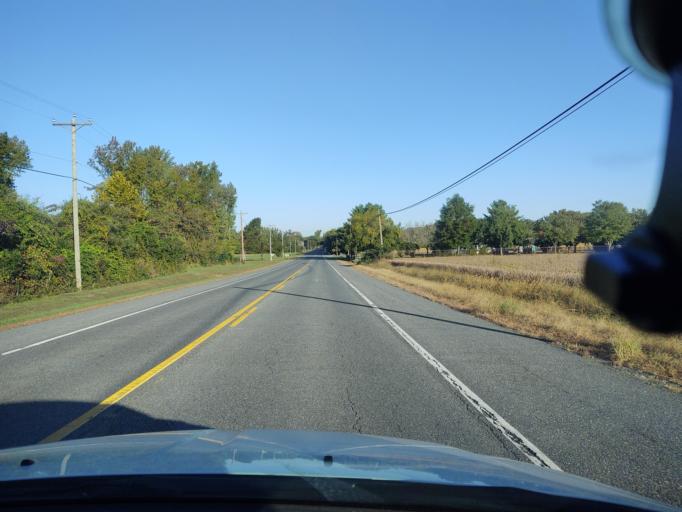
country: US
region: Maryland
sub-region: Queen Anne's County
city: Kingstown
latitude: 39.2356
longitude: -75.9168
